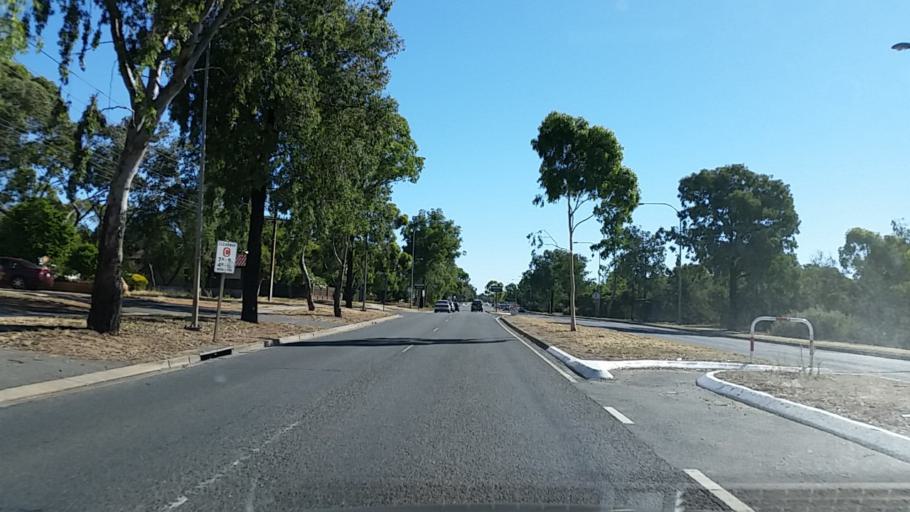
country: AU
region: South Australia
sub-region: Salisbury
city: Ingle Farm
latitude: -34.8219
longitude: 138.6379
